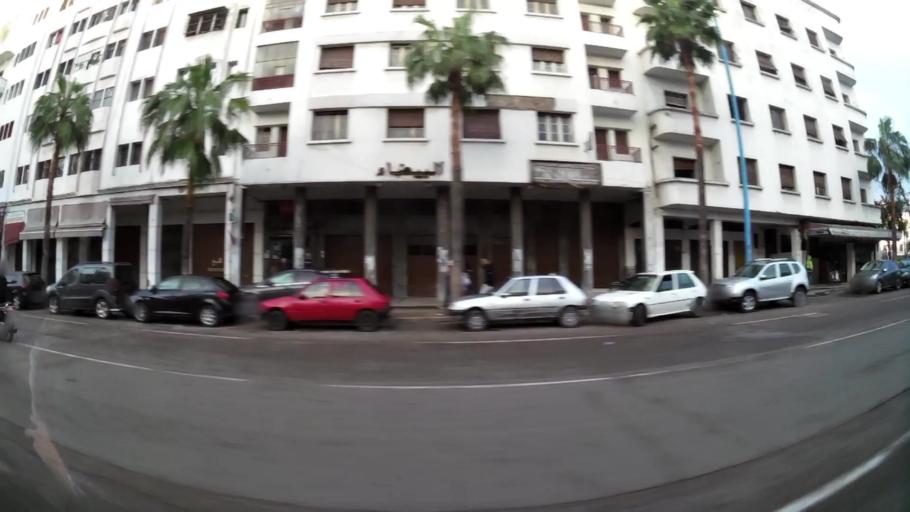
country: MA
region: Grand Casablanca
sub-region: Casablanca
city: Casablanca
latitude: 33.5659
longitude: -7.5953
